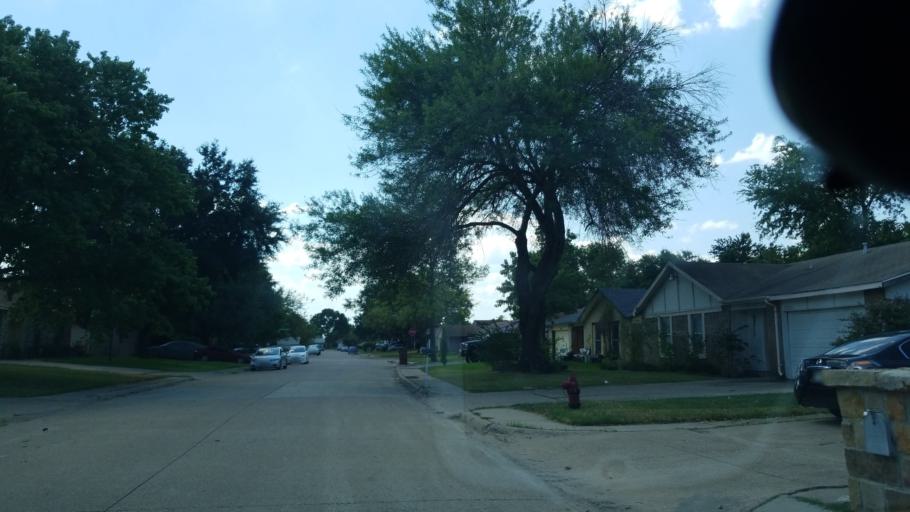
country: US
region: Texas
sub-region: Dallas County
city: Grand Prairie
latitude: 32.7134
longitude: -96.9924
